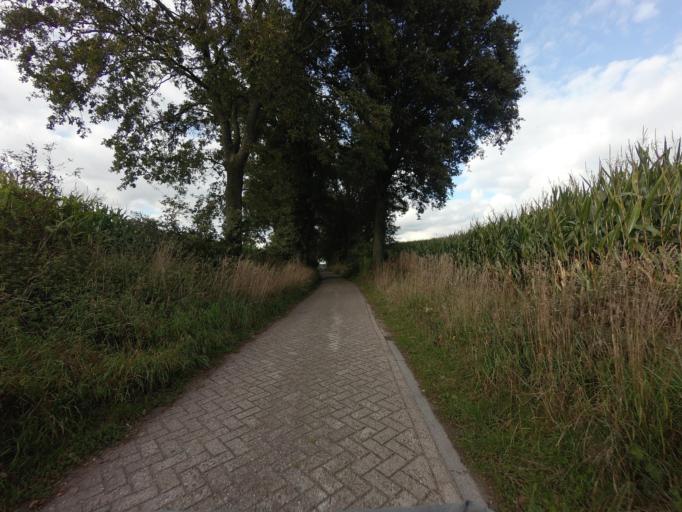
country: NL
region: Overijssel
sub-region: Gemeente Deventer
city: Schalkhaar
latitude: 52.2718
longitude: 6.2629
